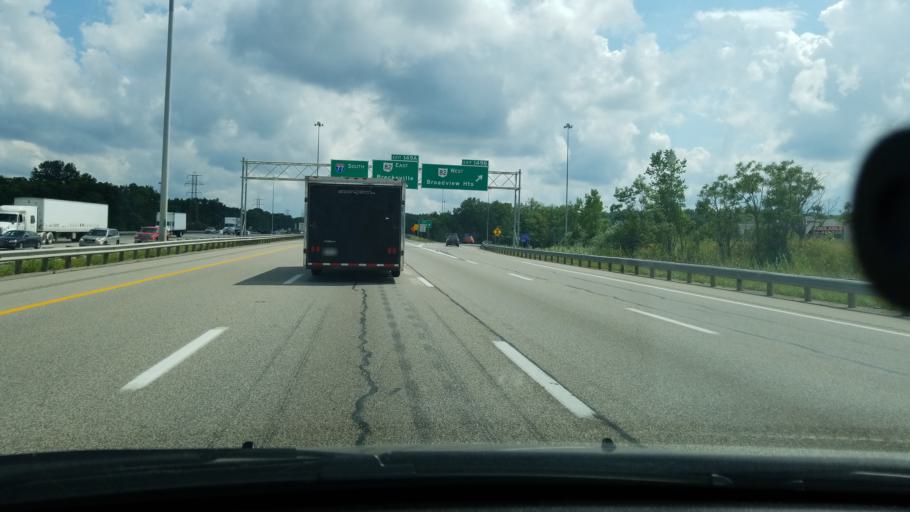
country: US
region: Ohio
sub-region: Cuyahoga County
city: Brecksville
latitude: 41.3190
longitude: -81.6491
